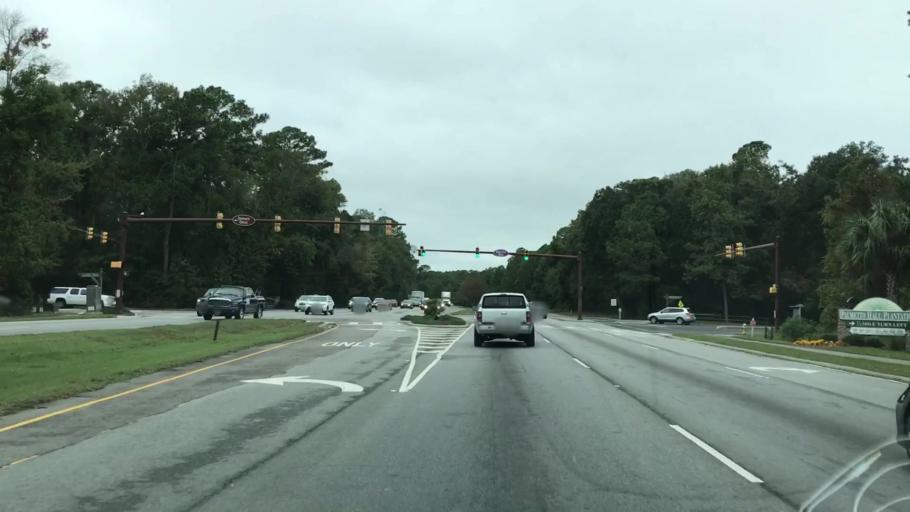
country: US
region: South Carolina
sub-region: Beaufort County
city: Hilton Head Island
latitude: 32.2170
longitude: -80.7115
